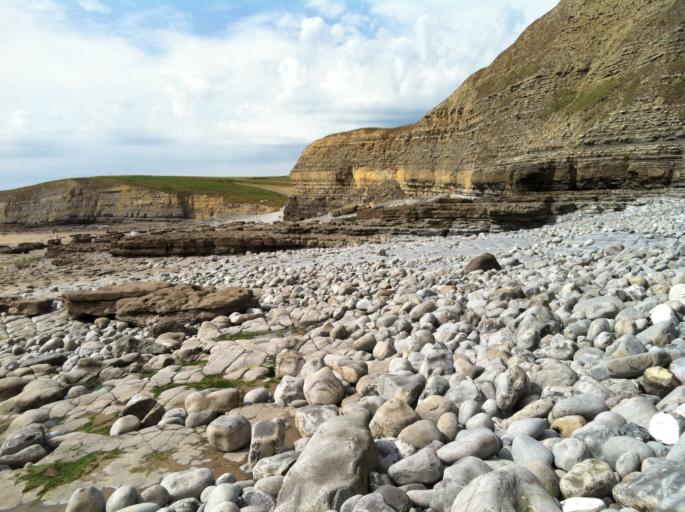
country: GB
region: Wales
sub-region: Bridgend county borough
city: Merthyr Mawr
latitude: 51.4430
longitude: -3.6045
